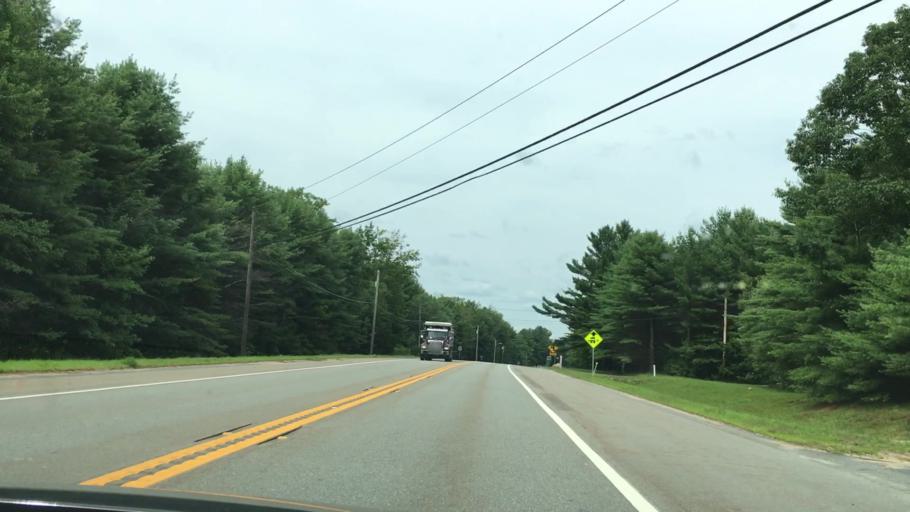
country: US
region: Massachusetts
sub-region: Worcester County
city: Gardner
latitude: 42.6322
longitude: -72.0073
